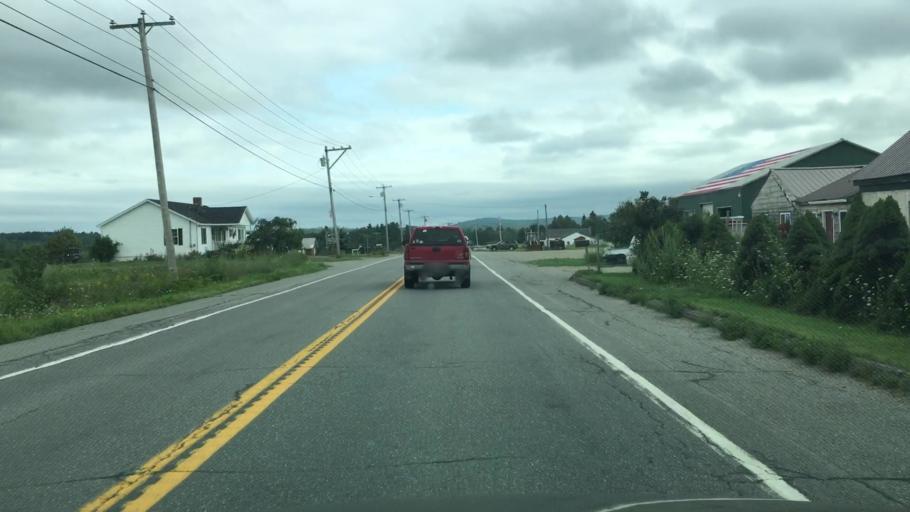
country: US
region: Maine
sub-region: Waldo County
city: Frankfort
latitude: 44.5653
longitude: -68.8673
